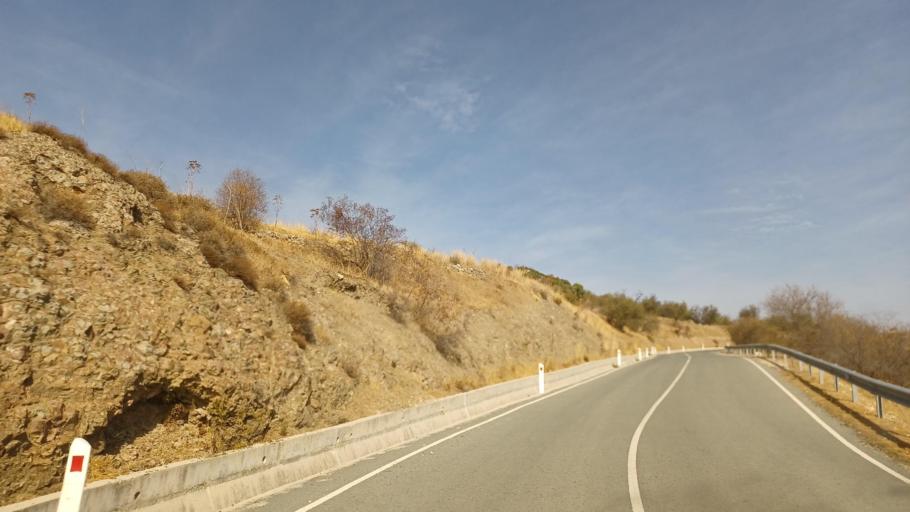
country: CY
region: Pafos
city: Polis
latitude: 34.9665
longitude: 32.5075
